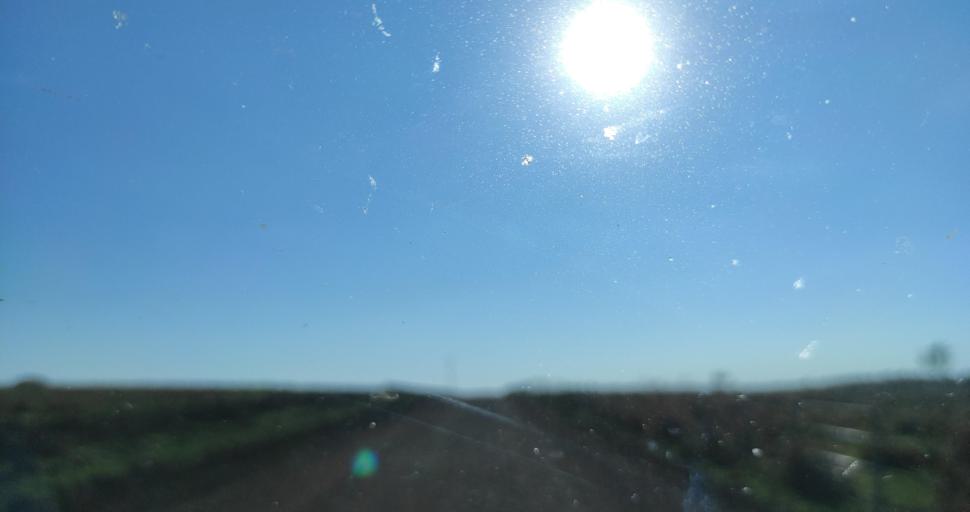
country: PY
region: Itapua
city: Carmen del Parana
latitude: -27.4158
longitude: -56.1333
